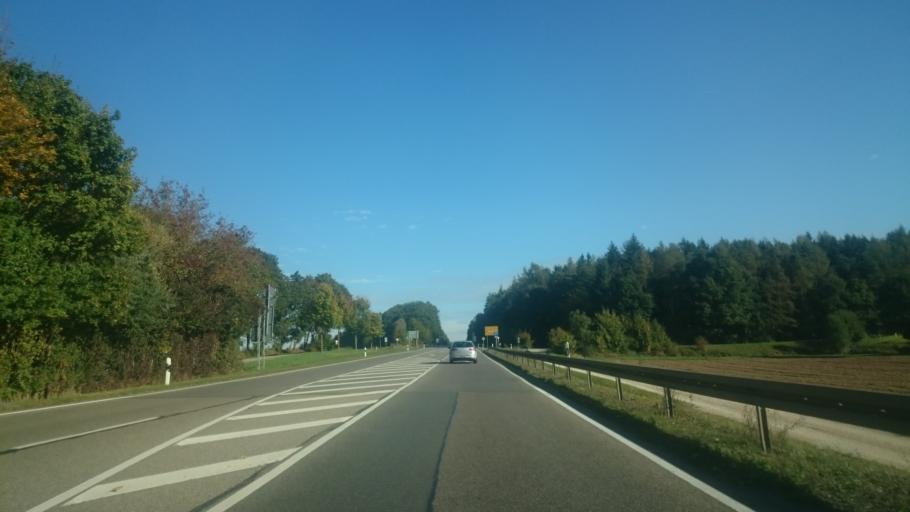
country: DE
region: Bavaria
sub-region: Regierungsbezirk Mittelfranken
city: Pleinfeld
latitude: 49.0827
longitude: 10.9752
